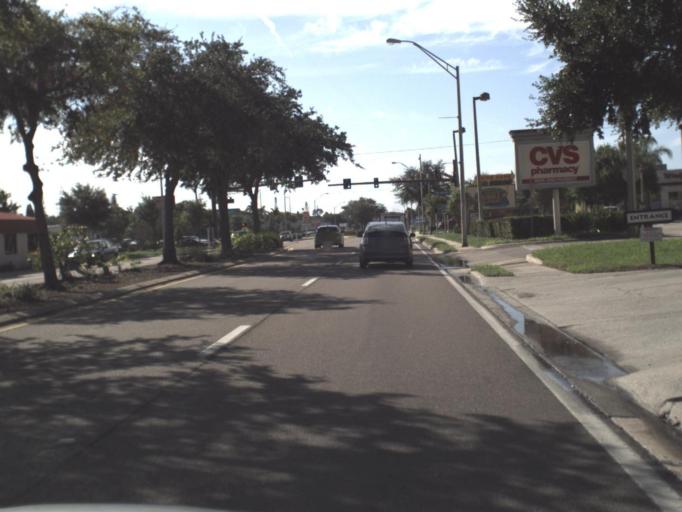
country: US
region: Florida
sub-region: Sarasota County
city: North Sarasota
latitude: 27.3682
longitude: -82.5521
